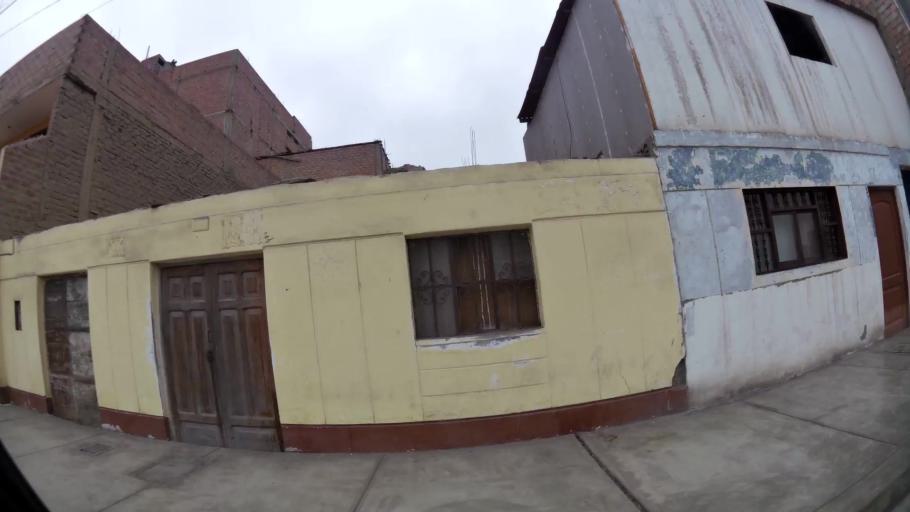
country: PE
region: Lima
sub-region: Barranca
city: Barranca
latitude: -10.7460
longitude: -77.7541
